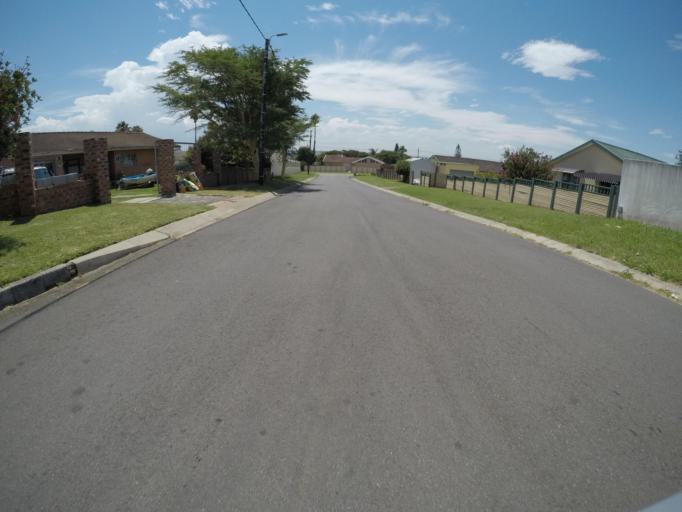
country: ZA
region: Eastern Cape
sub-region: Buffalo City Metropolitan Municipality
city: East London
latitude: -33.0329
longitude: 27.8508
